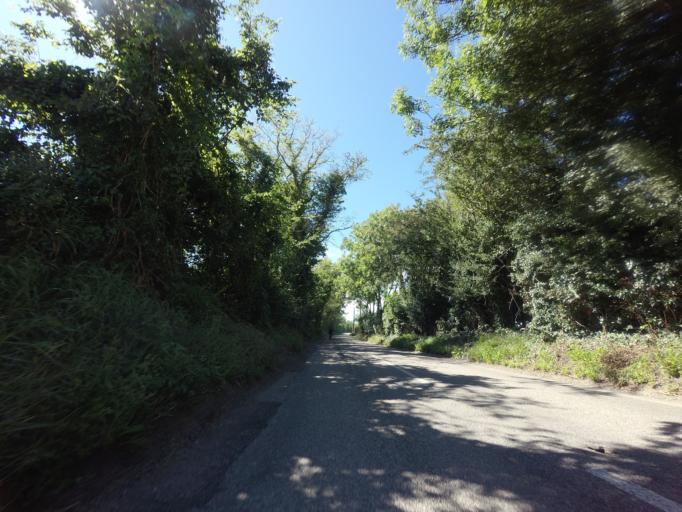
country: GB
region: England
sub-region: Kent
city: Westgate on Sea
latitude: 51.3326
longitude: 1.3415
